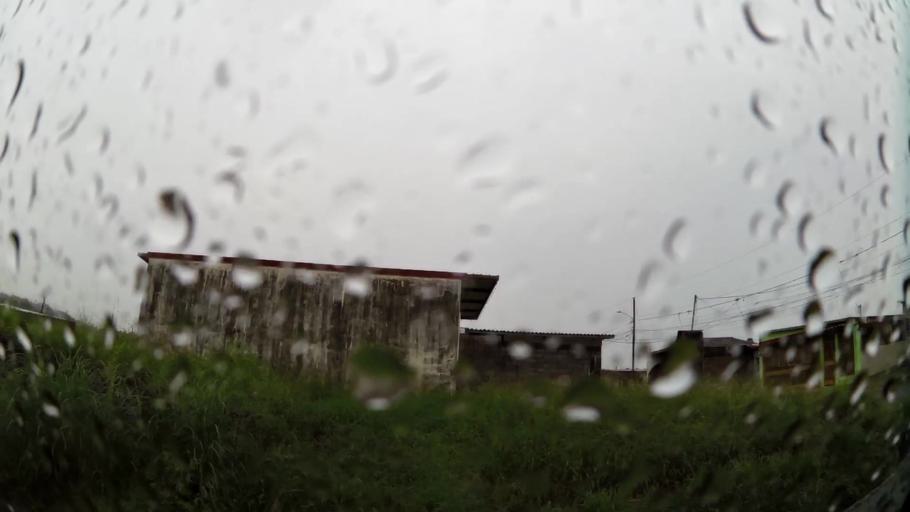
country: PA
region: Colon
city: Puerto Pilon
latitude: 9.3631
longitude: -79.8028
